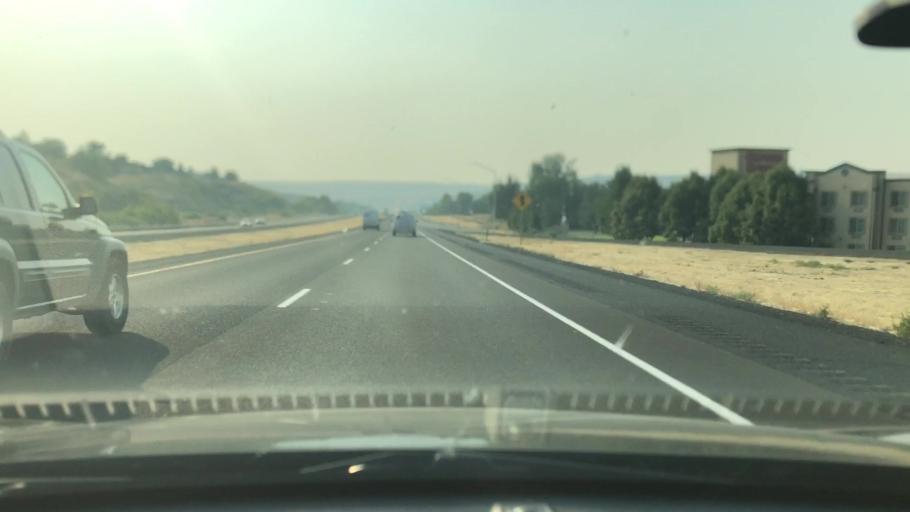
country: US
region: Oregon
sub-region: Umatilla County
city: Pendleton
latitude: 45.6642
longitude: -118.8096
